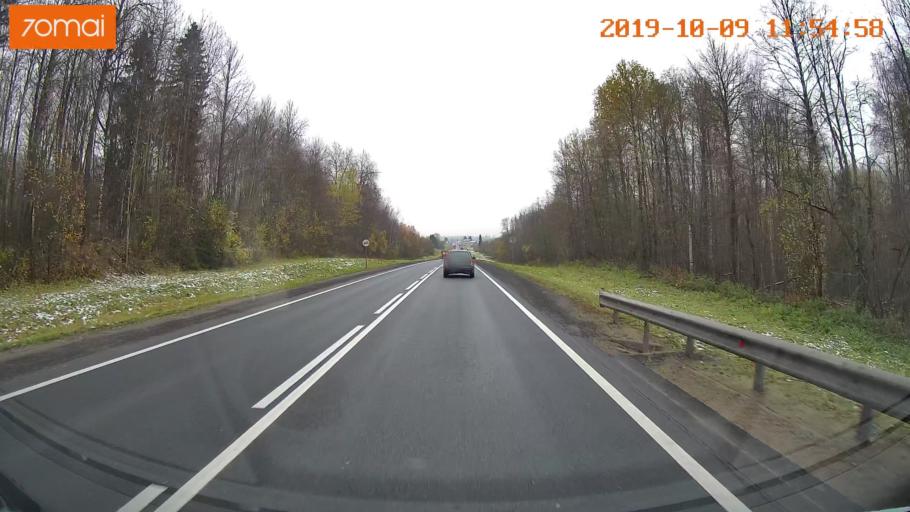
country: RU
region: Vologda
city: Gryazovets
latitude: 58.7529
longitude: 40.2839
